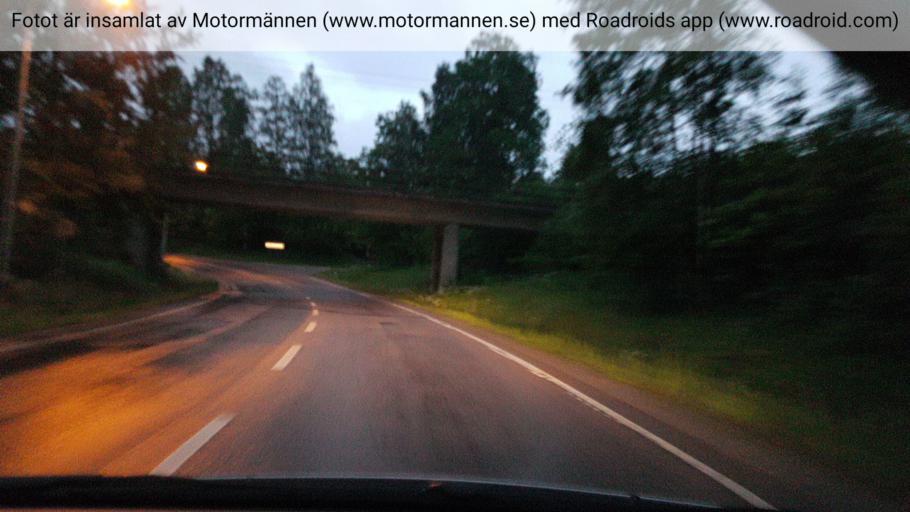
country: SE
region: Vaestmanland
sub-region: Skinnskattebergs Kommun
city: Skinnskatteberg
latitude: 59.8304
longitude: 15.6771
